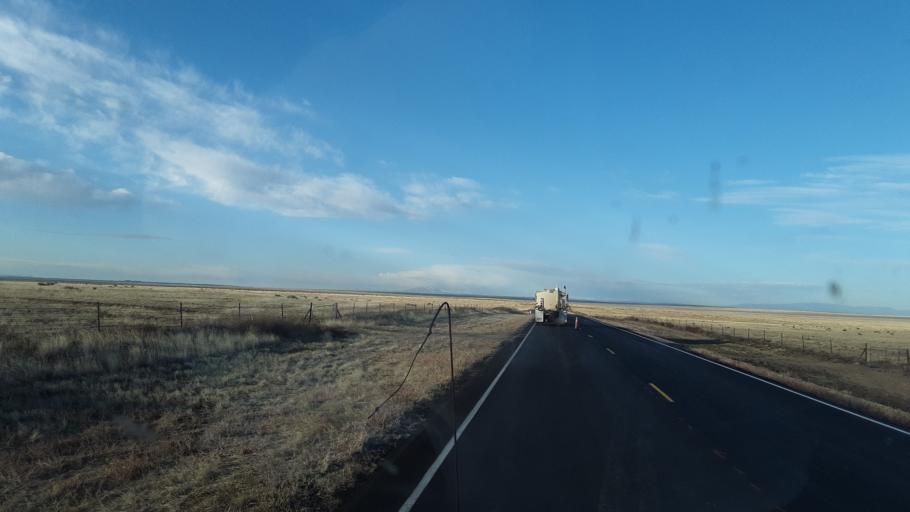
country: US
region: Colorado
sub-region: Otero County
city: Rocky Ford
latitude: 37.9639
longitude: -103.8391
